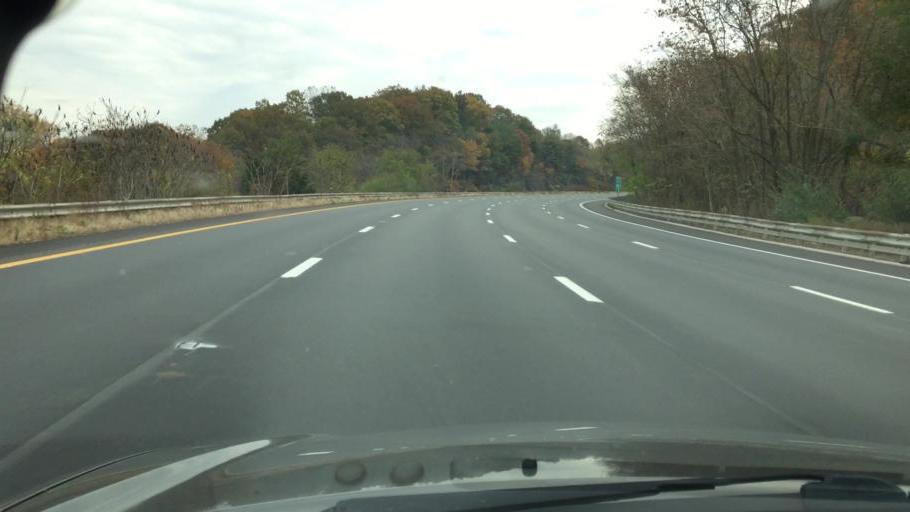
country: US
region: New Jersey
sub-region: Warren County
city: Belvidere
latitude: 40.9295
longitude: -75.0771
